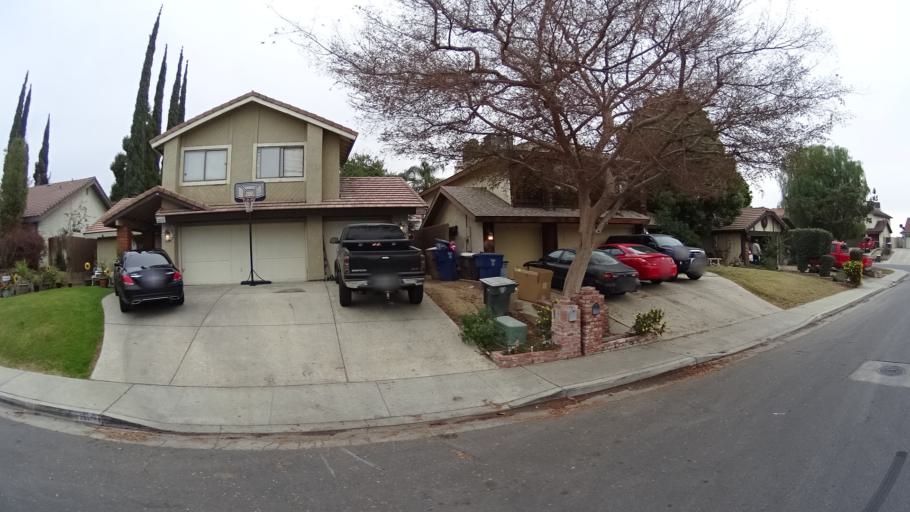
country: US
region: California
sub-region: Kern County
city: Bakersfield
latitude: 35.3806
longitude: -118.9364
